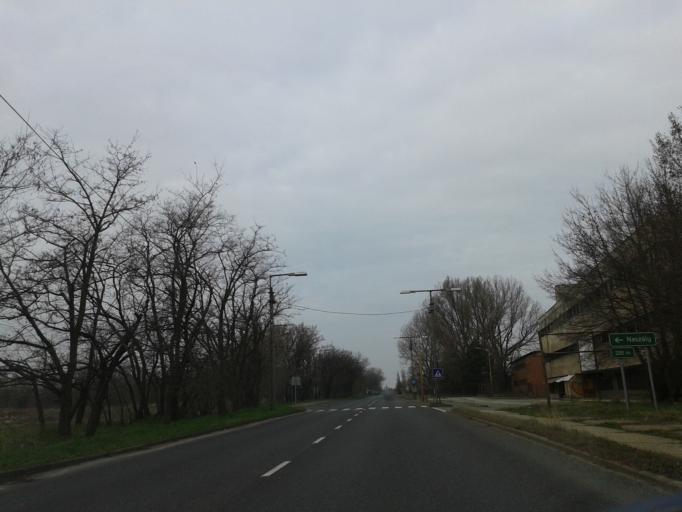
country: HU
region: Komarom-Esztergom
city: Almasfuzito
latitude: 47.7288
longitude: 18.2497
